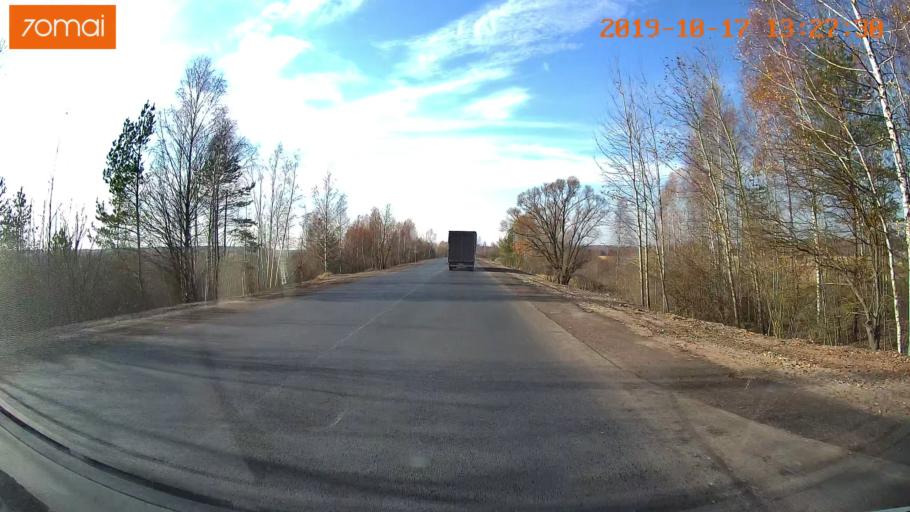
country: RU
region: Vladimir
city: Velikodvorskiy
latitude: 55.1134
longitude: 40.8936
